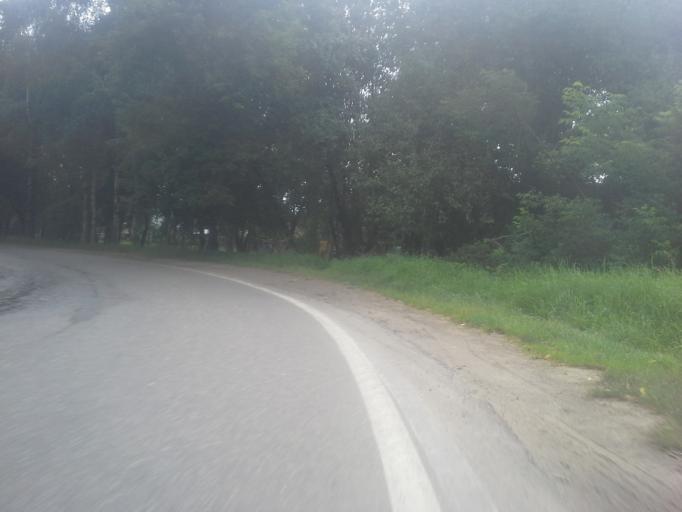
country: RU
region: Moskovskaya
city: Zvenigorod
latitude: 55.7261
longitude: 36.8345
